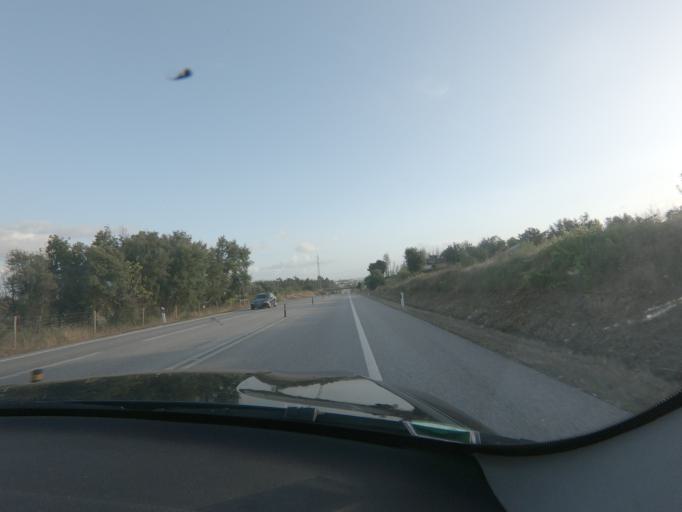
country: PT
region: Viseu
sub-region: Santa Comba Dao
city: Santa Comba Dao
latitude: 40.3708
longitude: -8.1286
